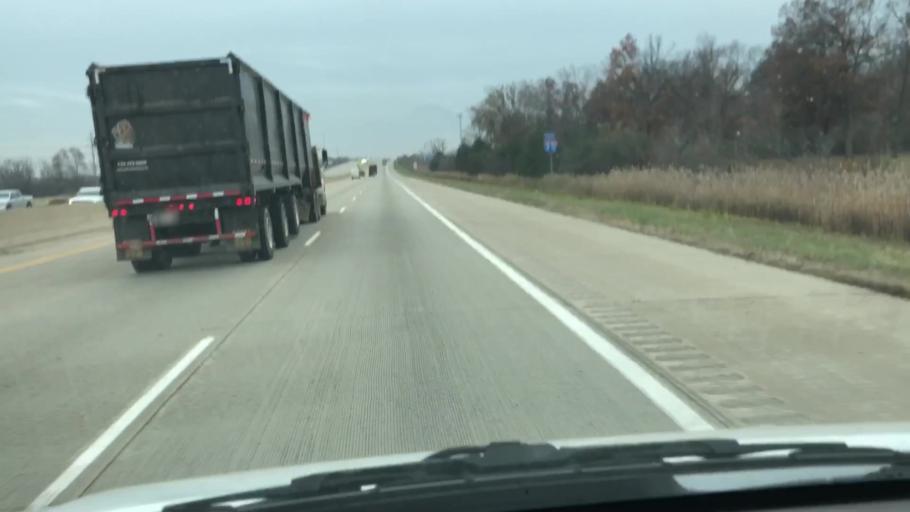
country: US
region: Michigan
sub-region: Wayne County
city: Woodhaven
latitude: 42.1308
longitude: -83.2415
